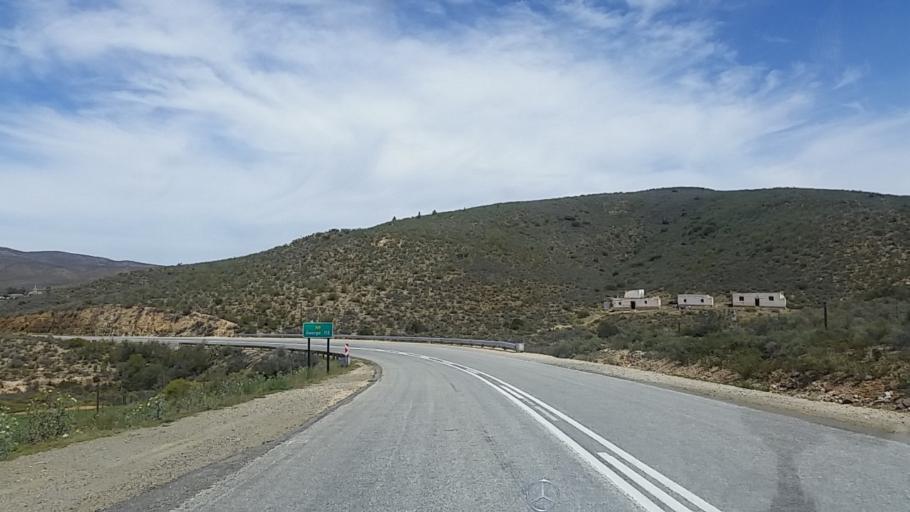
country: ZA
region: Western Cape
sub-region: Eden District Municipality
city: Knysna
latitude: -33.6422
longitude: 23.1338
